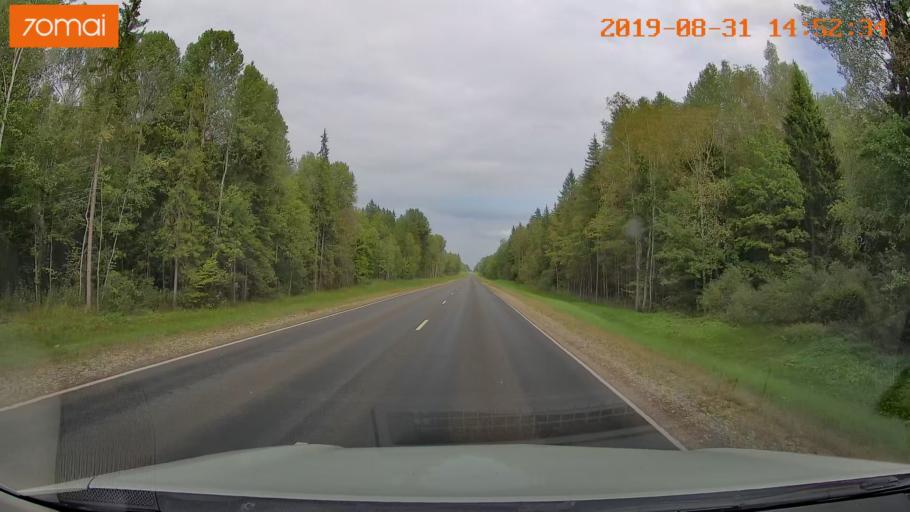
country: RU
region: Kaluga
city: Spas-Demensk
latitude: 54.2769
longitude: 33.8428
